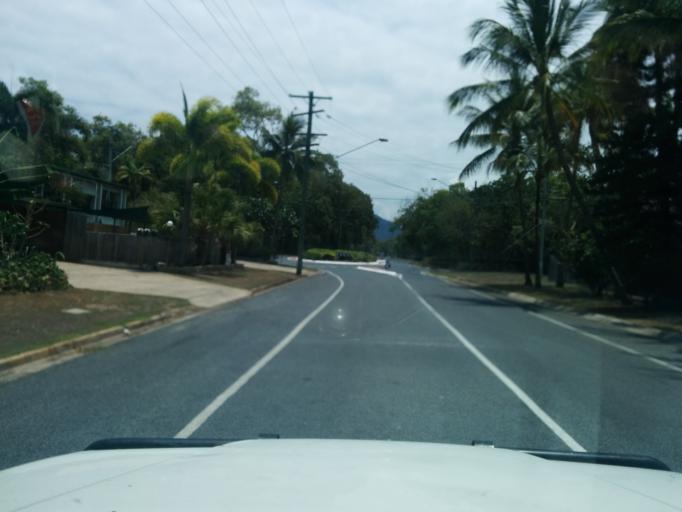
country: AU
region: Queensland
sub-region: Cairns
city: Yorkeys Knob
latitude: -16.8413
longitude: 145.7356
